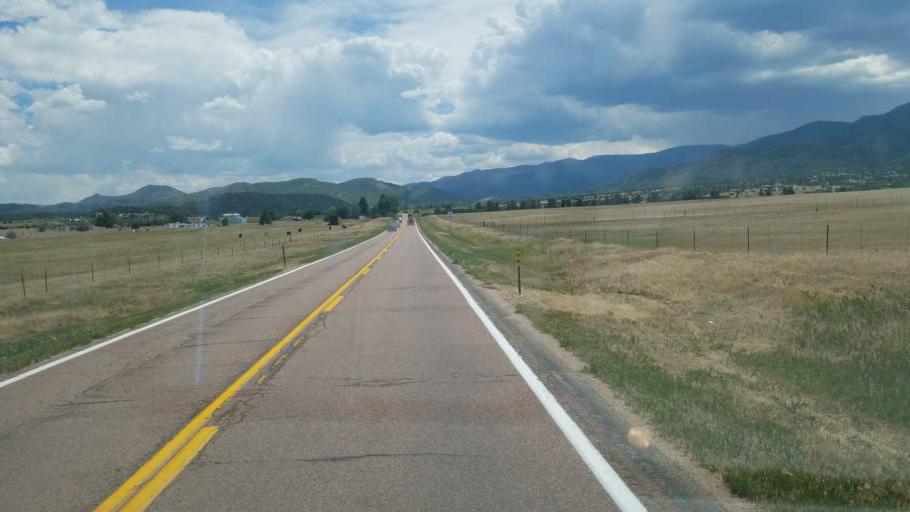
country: US
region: Colorado
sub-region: Fremont County
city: Florence
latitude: 38.2526
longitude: -105.0903
